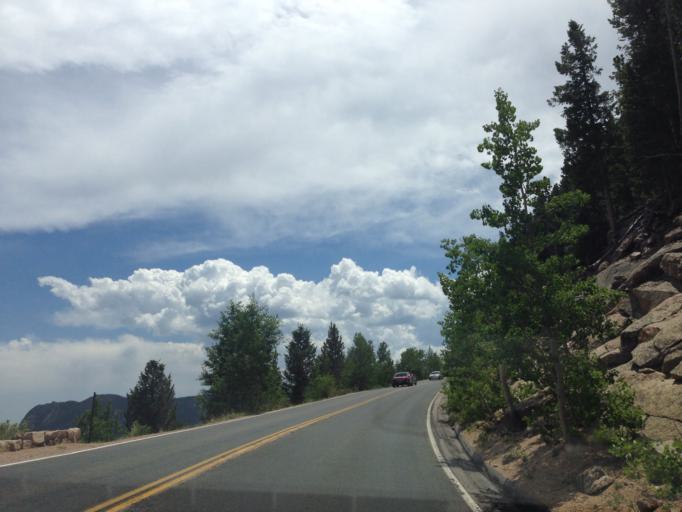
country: US
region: Colorado
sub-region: Larimer County
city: Estes Park
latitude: 40.3933
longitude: -105.6356
